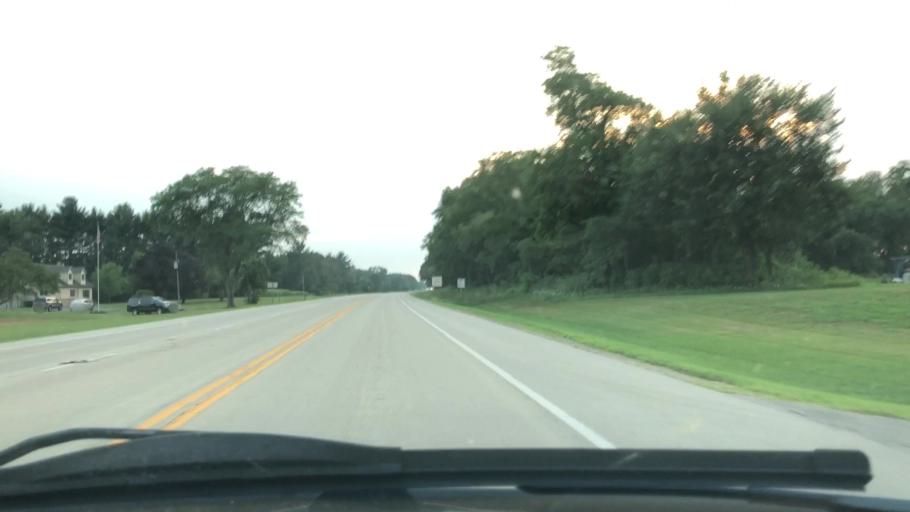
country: US
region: Wisconsin
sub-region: Sauk County
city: Spring Green
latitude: 43.1896
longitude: -90.1346
